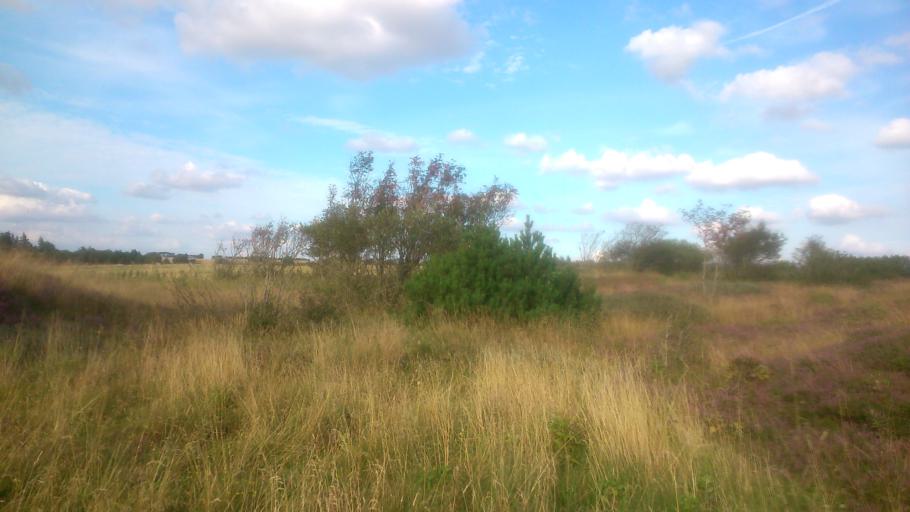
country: DK
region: Central Jutland
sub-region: Ringkobing-Skjern Kommune
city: Skjern
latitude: 56.0288
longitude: 8.4414
